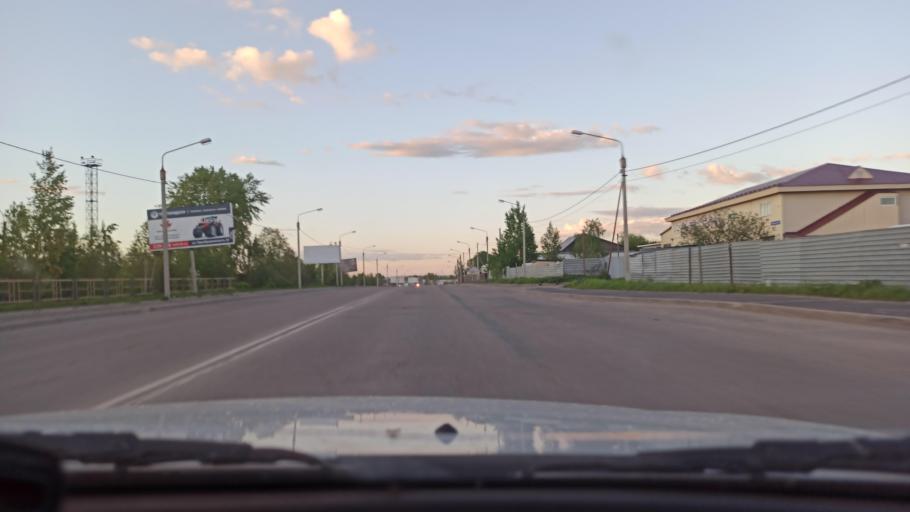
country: RU
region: Vologda
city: Vologda
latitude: 59.2174
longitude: 39.8176
